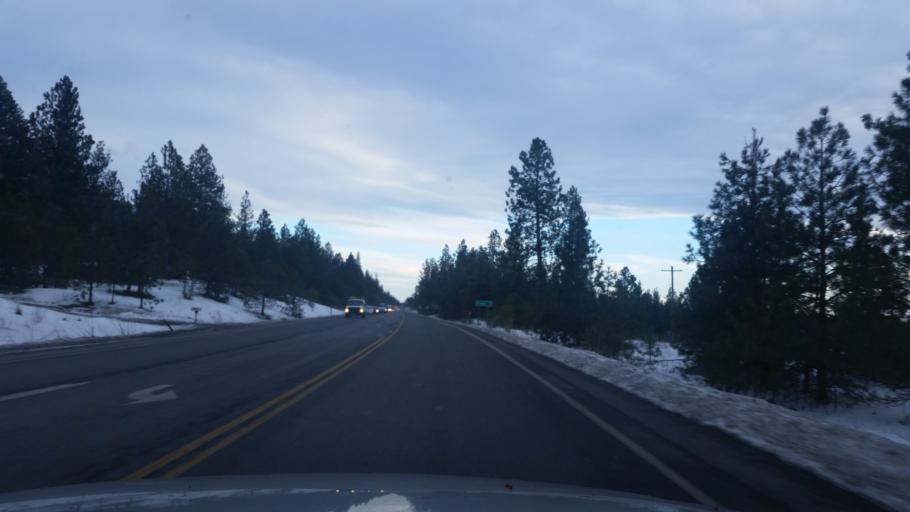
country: US
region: Washington
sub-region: Spokane County
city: Cheney
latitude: 47.5544
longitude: -117.5934
